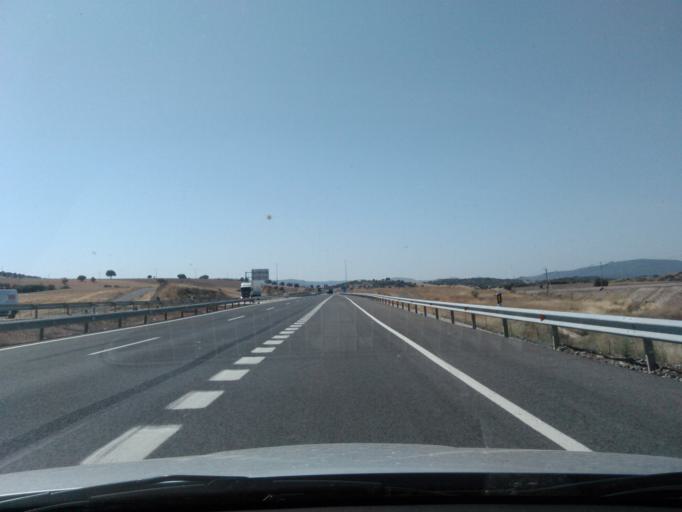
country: ES
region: Castille-La Mancha
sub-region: Provincia de Ciudad Real
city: Viso del Marques
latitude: 38.4921
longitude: -3.5027
